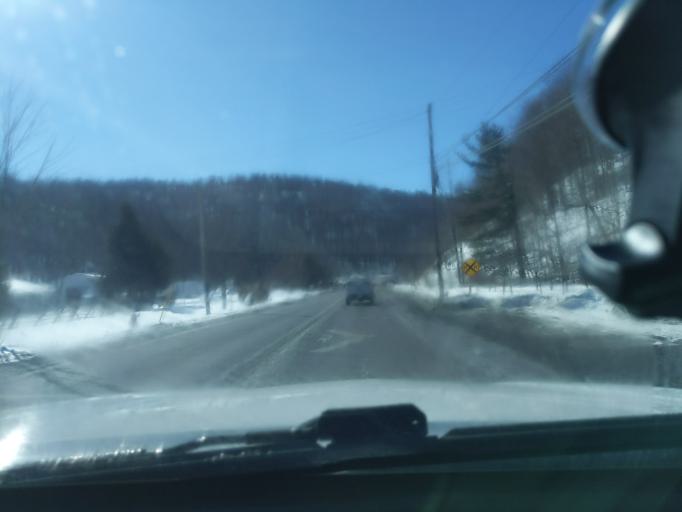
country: US
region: Maryland
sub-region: Allegany County
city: Lonaconing
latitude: 39.5543
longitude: -78.9901
